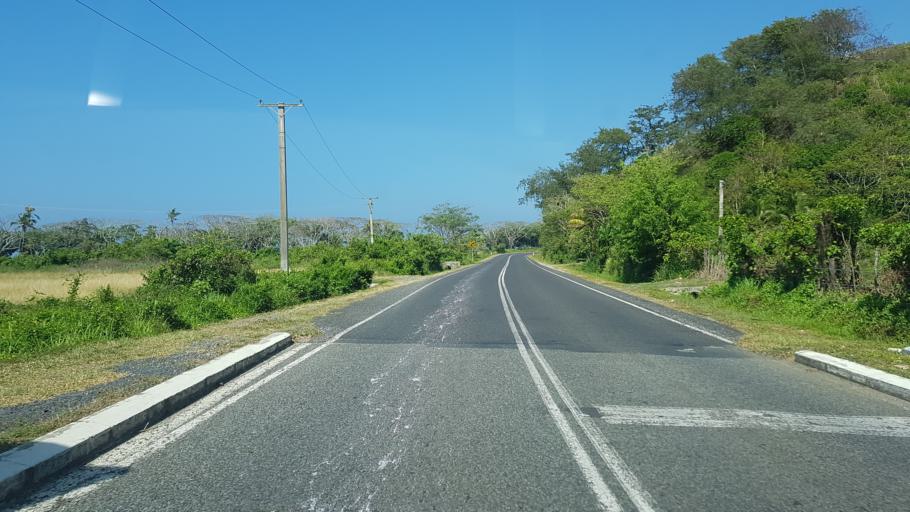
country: FJ
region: Western
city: Nadi
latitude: -18.1838
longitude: 177.6023
